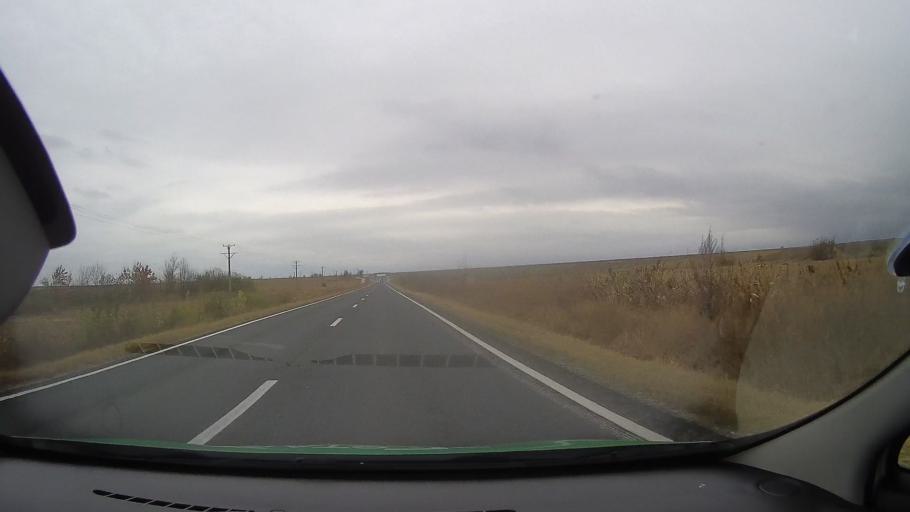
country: RO
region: Constanta
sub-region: Comuna Nicolae Balcescu
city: Nicolae Balcescu
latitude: 44.3844
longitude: 28.3956
